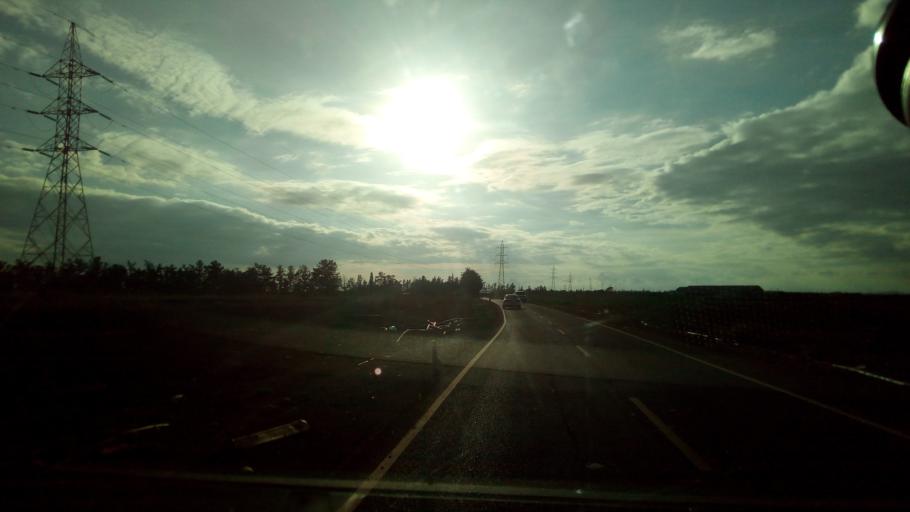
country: CY
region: Ammochostos
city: Avgorou
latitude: 35.0117
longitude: 33.8144
